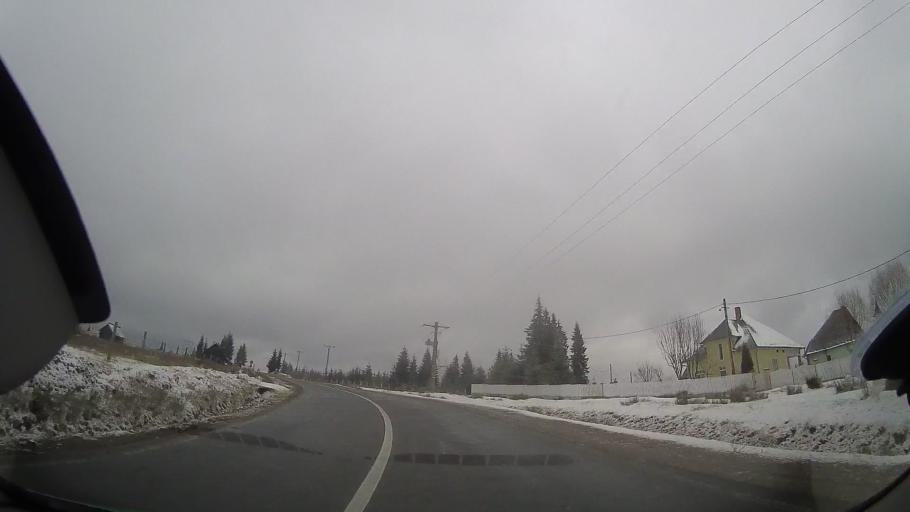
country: RO
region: Cluj
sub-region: Comuna Belis
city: Belis
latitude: 46.6924
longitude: 23.0400
